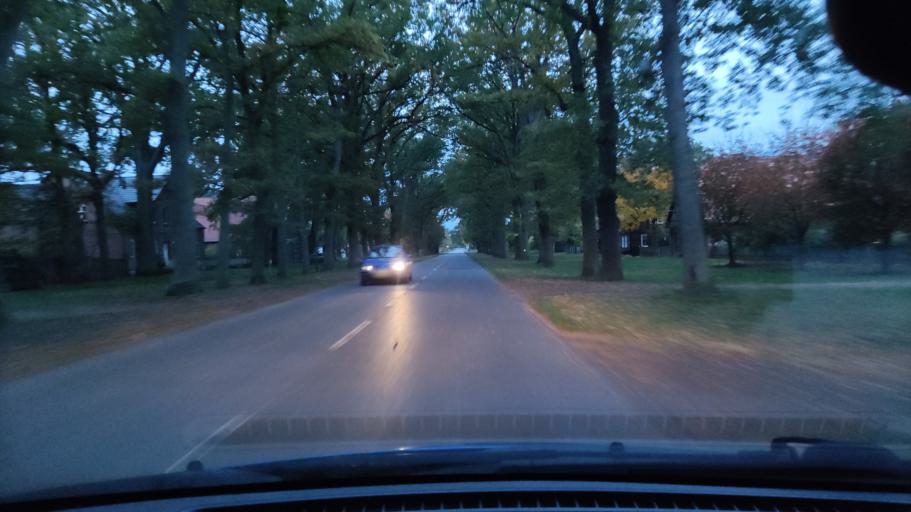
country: DE
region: Lower Saxony
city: Trebel
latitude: 52.9588
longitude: 11.3288
